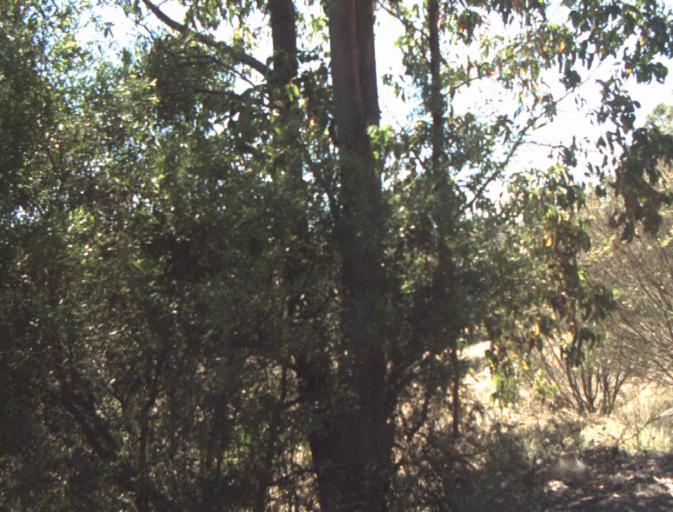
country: AU
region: Tasmania
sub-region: Dorset
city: Scottsdale
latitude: -41.3595
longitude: 147.4022
